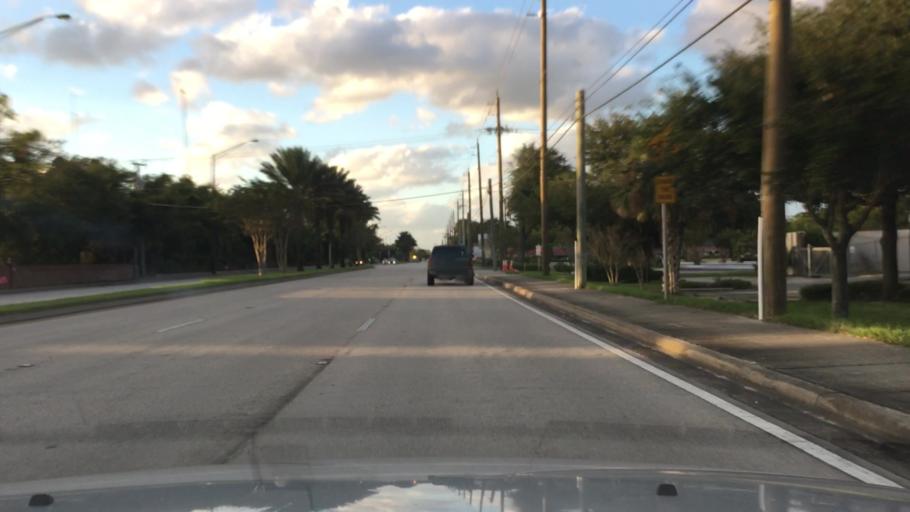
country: US
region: Florida
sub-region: Volusia County
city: Ormond Beach
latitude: 29.2671
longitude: -81.0789
